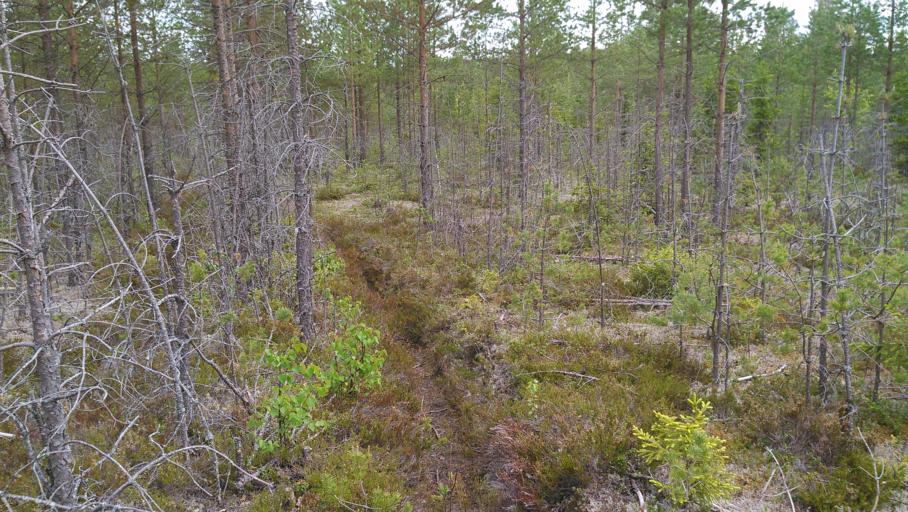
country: SE
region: Vaesterbotten
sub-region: Vannas Kommun
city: Vannasby
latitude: 64.0156
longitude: 19.9141
